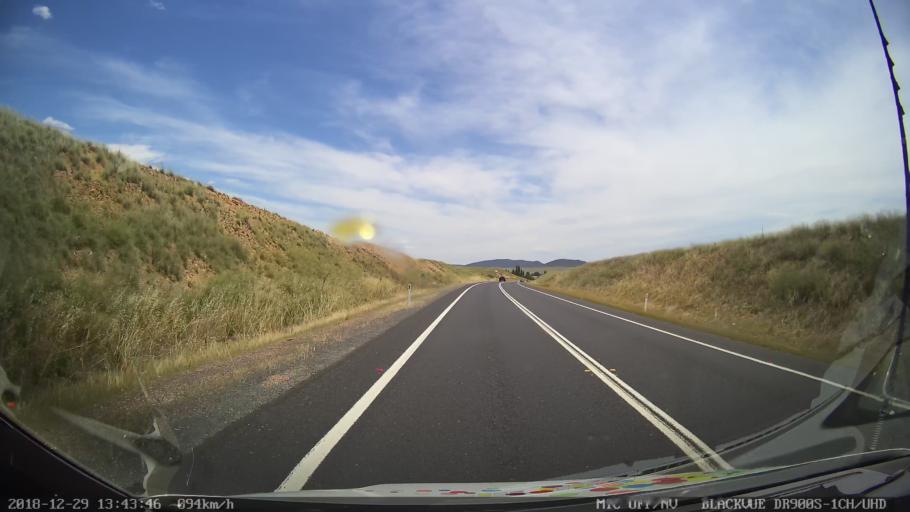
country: AU
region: New South Wales
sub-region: Cooma-Monaro
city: Cooma
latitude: -36.0772
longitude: 149.1598
